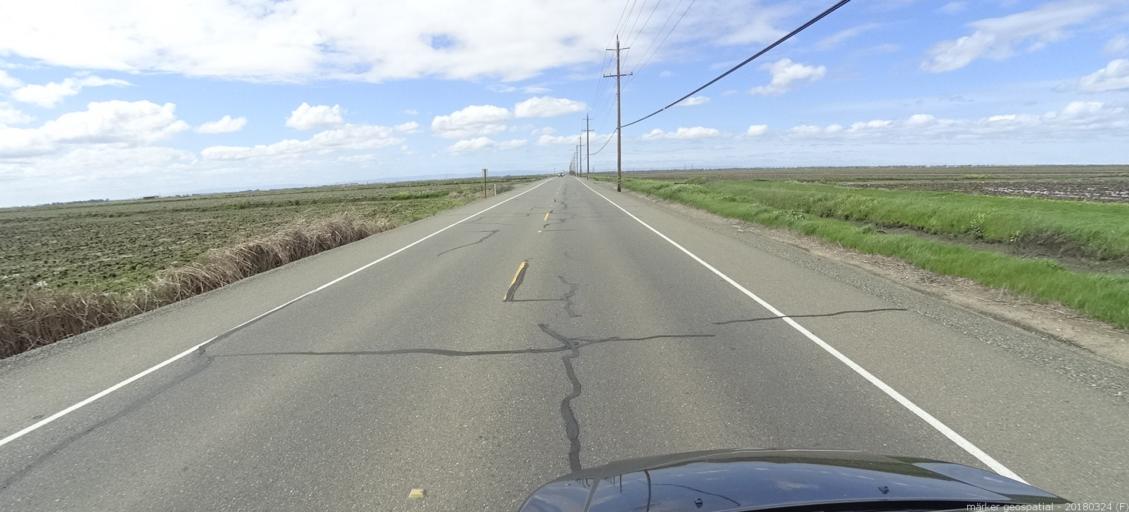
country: US
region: California
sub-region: Sacramento County
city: Elverta
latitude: 38.7143
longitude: -121.5200
